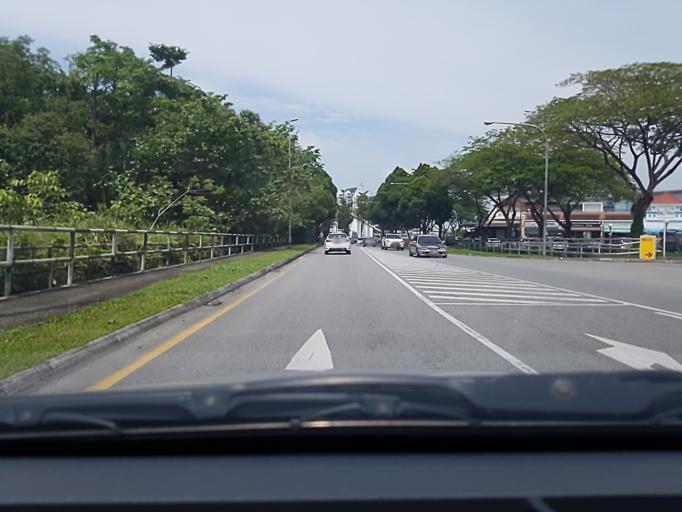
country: MY
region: Sarawak
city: Kuching
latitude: 1.5186
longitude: 110.3678
